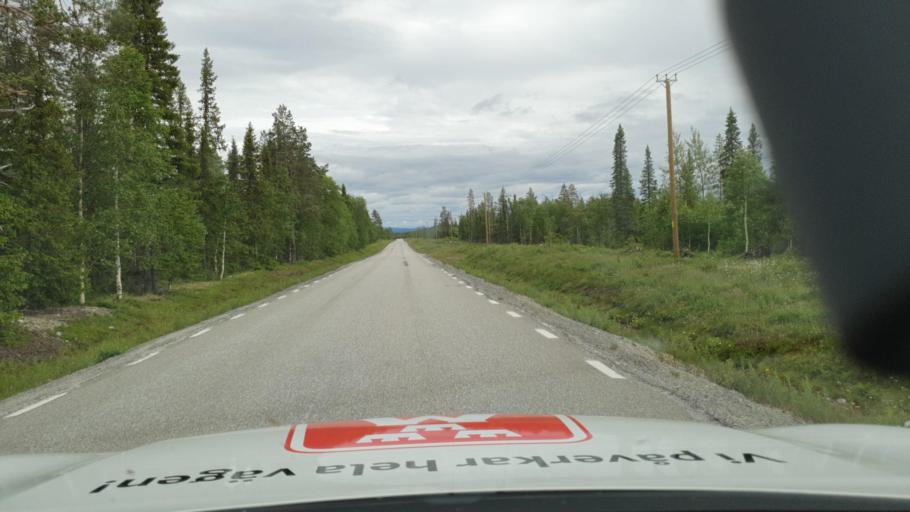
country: SE
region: Vaesterbotten
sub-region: Lycksele Kommun
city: Soderfors
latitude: 64.3876
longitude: 18.0096
